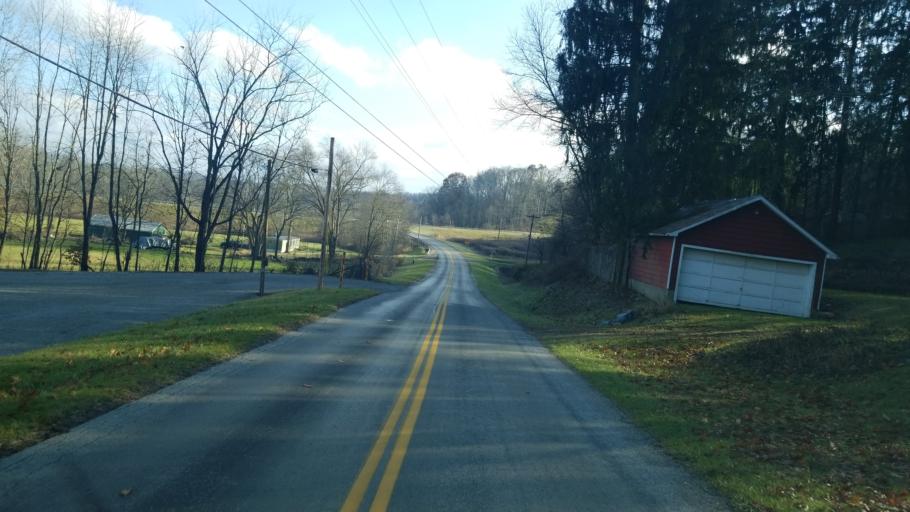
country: US
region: Ohio
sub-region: Ashland County
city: Loudonville
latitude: 40.6605
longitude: -82.3220
